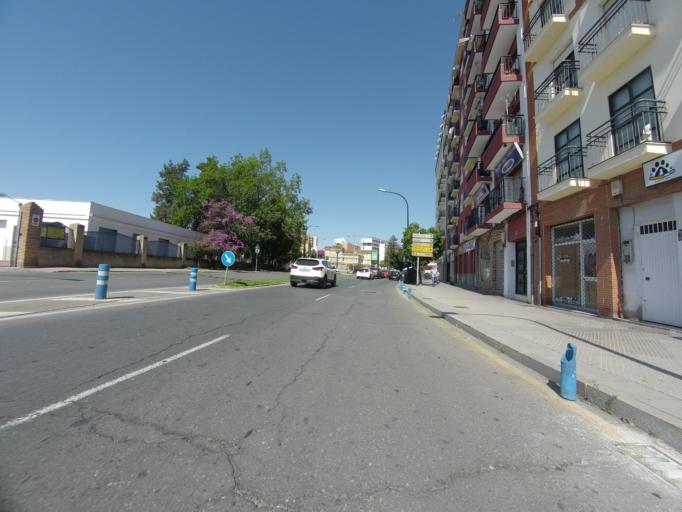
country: ES
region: Andalusia
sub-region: Provincia de Huelva
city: Huelva
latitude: 37.2534
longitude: -6.9499
